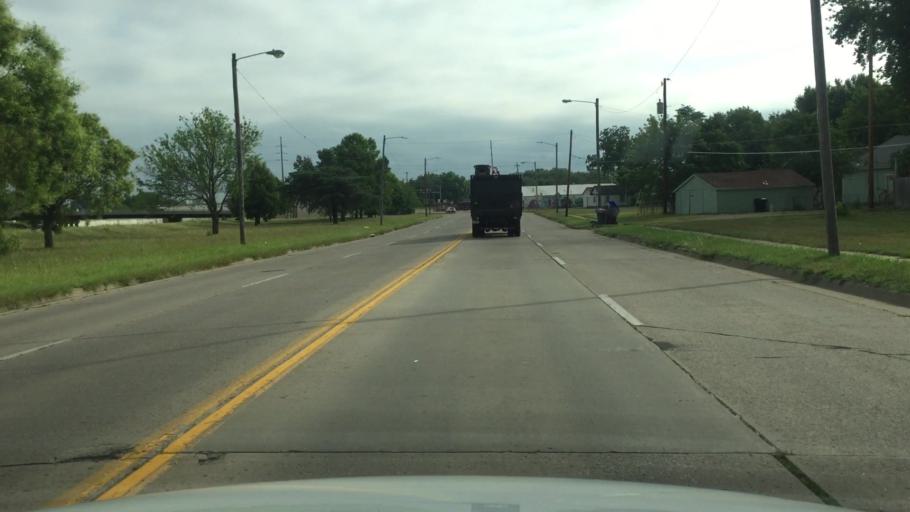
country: US
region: Kansas
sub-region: Shawnee County
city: Topeka
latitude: 39.0466
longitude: -95.6630
